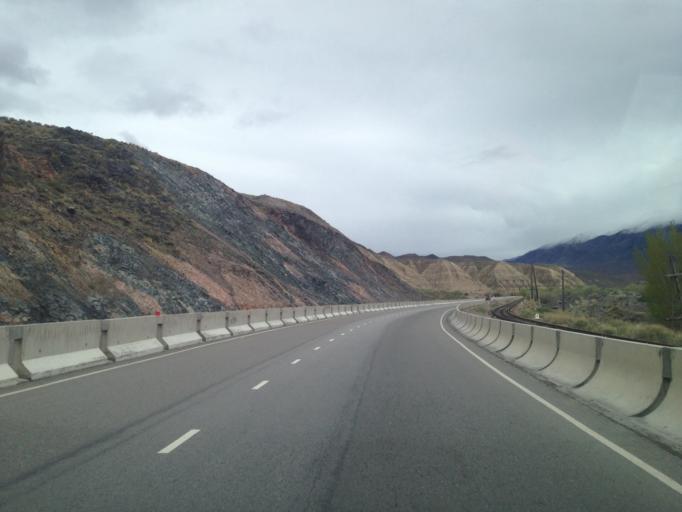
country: KG
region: Naryn
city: Kochkor
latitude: 42.4954
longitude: 75.8471
